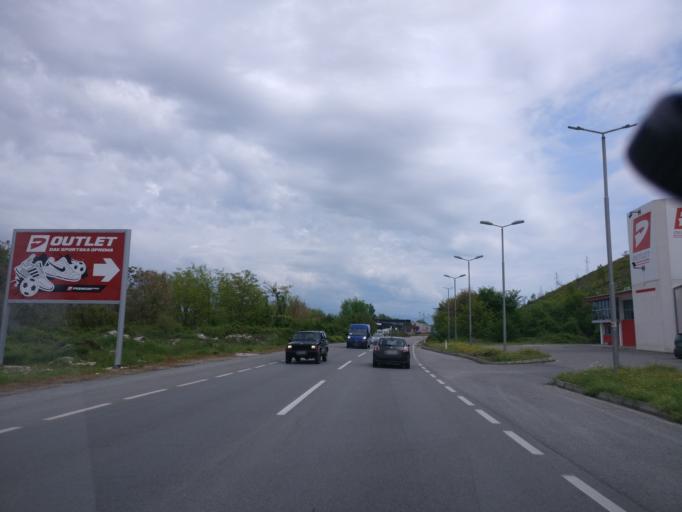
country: ME
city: Spuz
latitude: 42.4540
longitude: 19.1926
